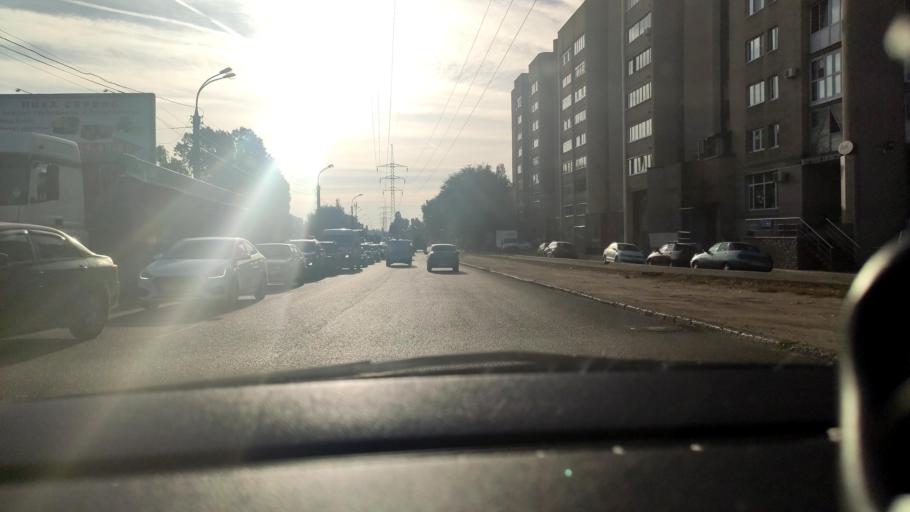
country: RU
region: Voronezj
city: Voronezh
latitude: 51.6403
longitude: 39.1601
